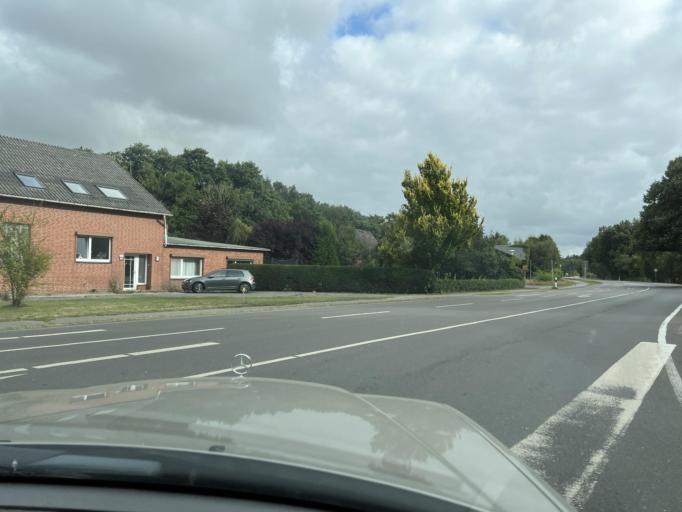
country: DE
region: Schleswig-Holstein
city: Stelle-Wittenwurth
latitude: 54.2712
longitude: 9.0475
